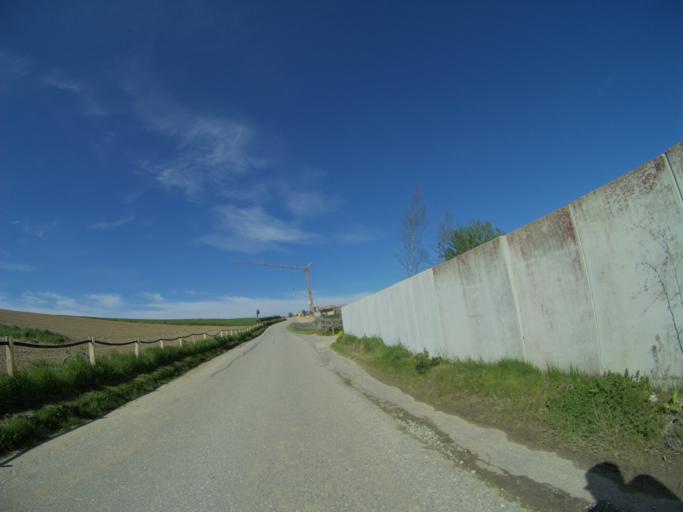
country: DE
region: Bavaria
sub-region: Upper Bavaria
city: Marzling
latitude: 48.4222
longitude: 11.7753
